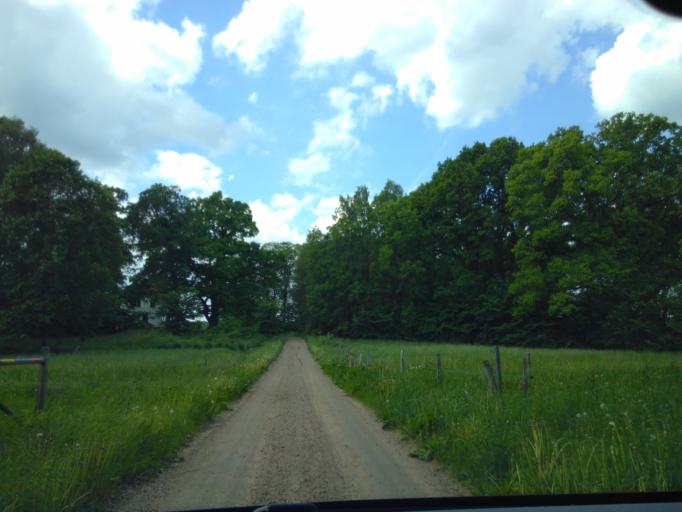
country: SE
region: Vaestra Goetaland
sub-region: Herrljunga Kommun
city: Herrljunga
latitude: 58.0737
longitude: 13.0029
